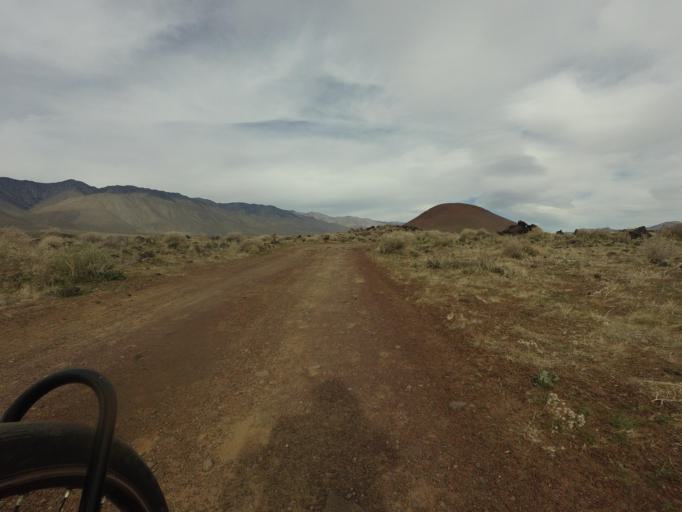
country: US
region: California
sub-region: Kern County
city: Inyokern
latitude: 35.9748
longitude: -117.9125
